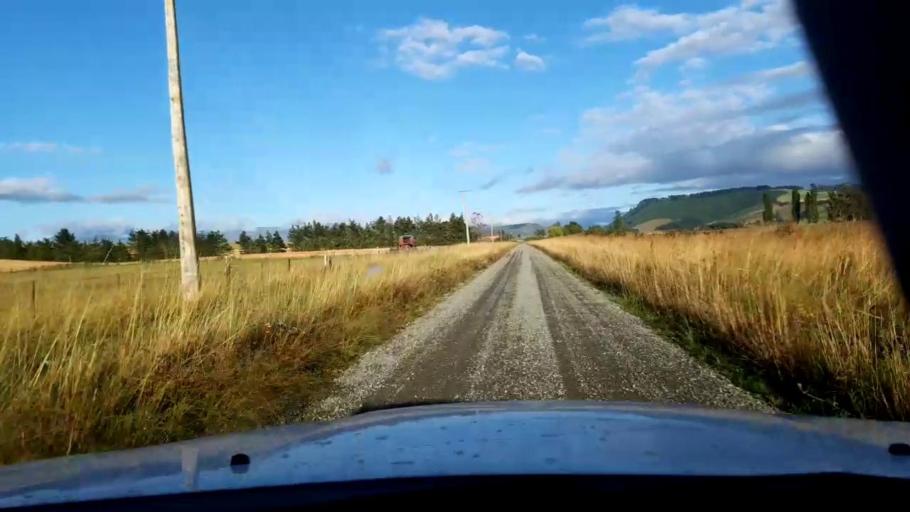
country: NZ
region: Canterbury
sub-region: Timaru District
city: Timaru
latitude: -44.4302
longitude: 171.1288
